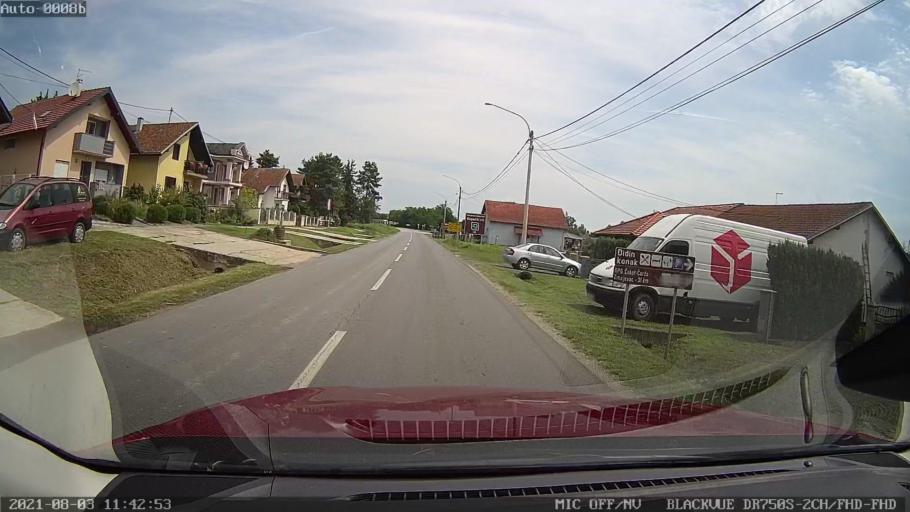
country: HR
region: Osjecko-Baranjska
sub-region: Grad Osijek
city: Bilje
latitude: 45.6074
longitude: 18.7543
